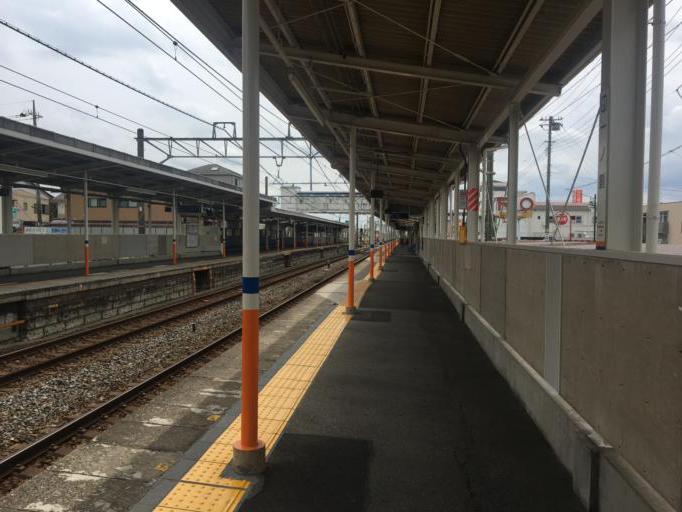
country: JP
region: Saitama
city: Kasukabe
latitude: 35.9650
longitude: 139.7658
